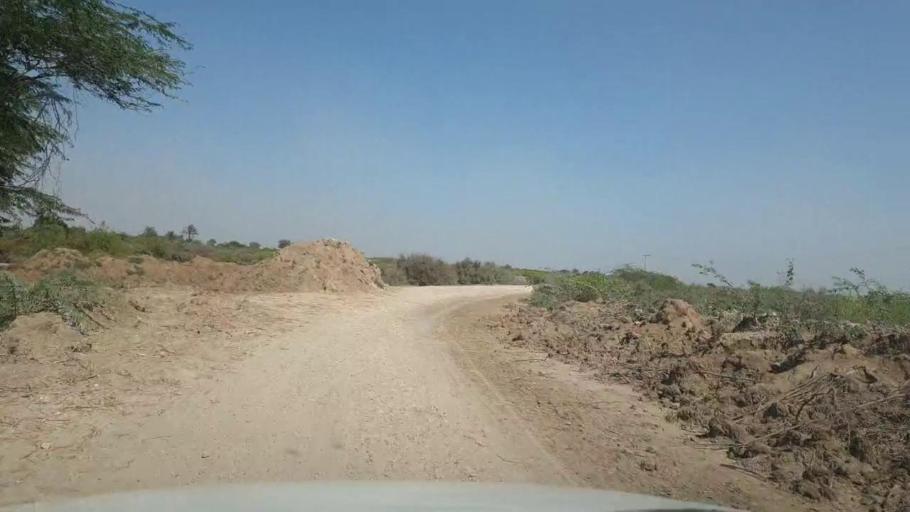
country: PK
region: Sindh
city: Mirpur Sakro
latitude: 24.3995
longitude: 67.7578
